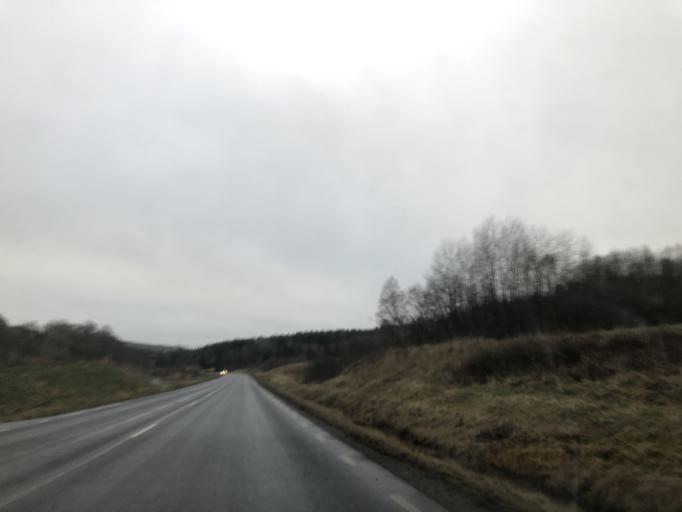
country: SE
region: Vaestra Goetaland
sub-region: Ulricehamns Kommun
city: Ulricehamn
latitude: 57.8258
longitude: 13.2885
